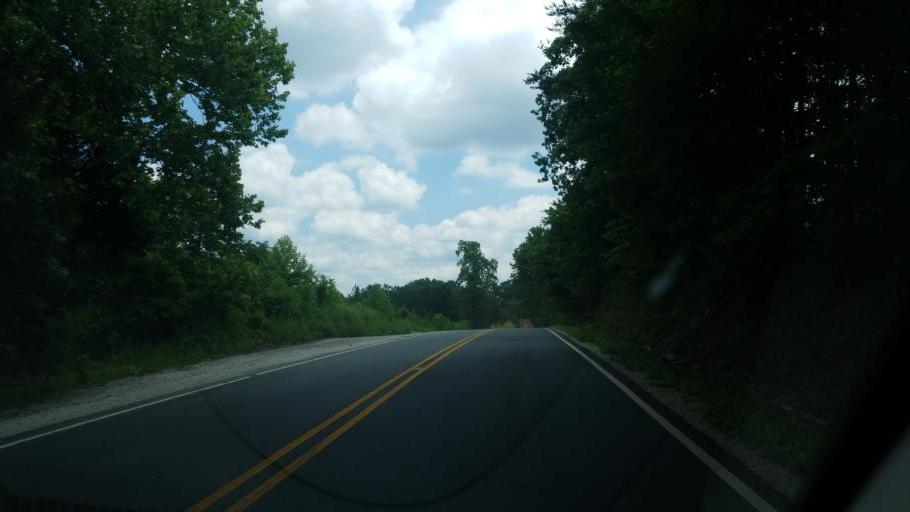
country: US
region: Virginia
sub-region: Amherst County
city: Amherst
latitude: 37.5739
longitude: -78.8814
